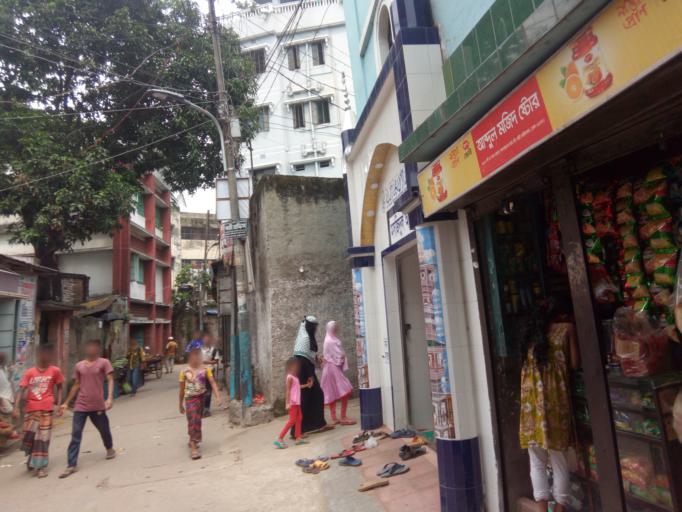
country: BD
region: Dhaka
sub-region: Dhaka
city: Dhaka
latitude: 23.6960
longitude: 90.4232
